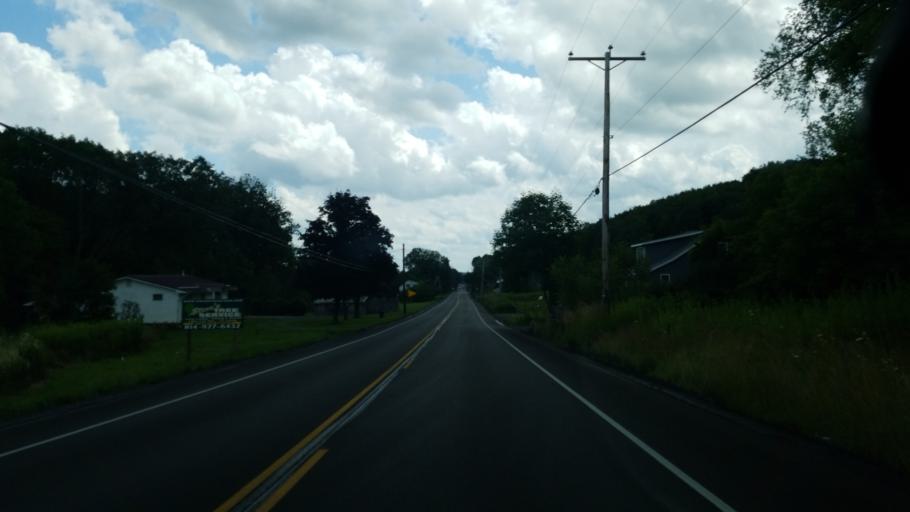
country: US
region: Pennsylvania
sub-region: Jefferson County
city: Brookville
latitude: 41.2402
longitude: -79.1109
